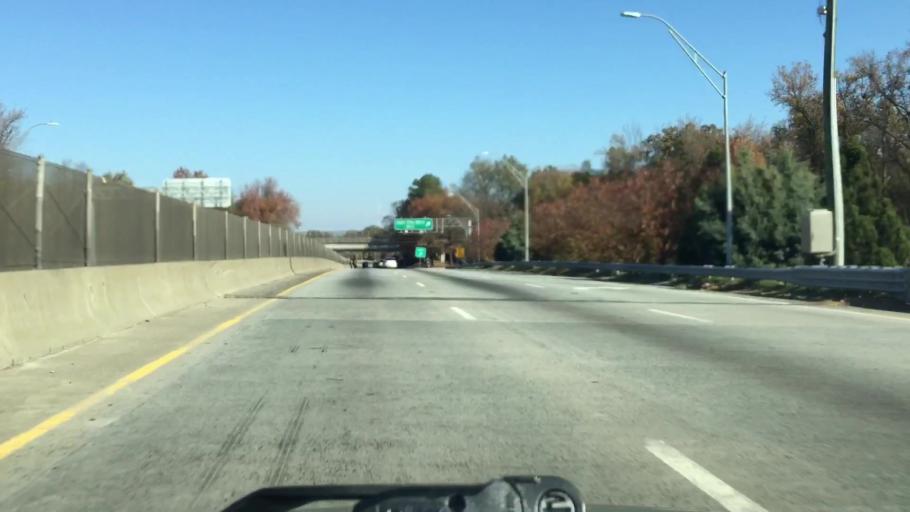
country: US
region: North Carolina
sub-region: Guilford County
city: Greensboro
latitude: 36.0638
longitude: -79.7673
